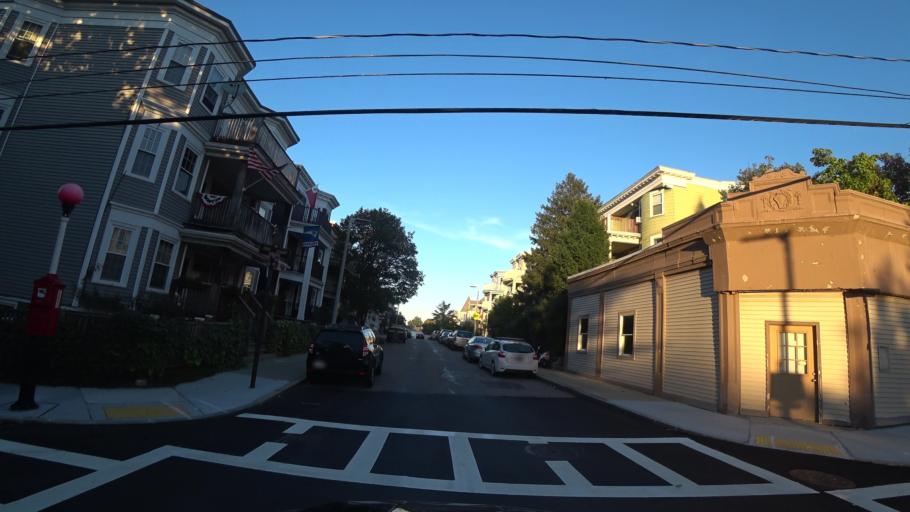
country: US
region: Massachusetts
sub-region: Suffolk County
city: South Boston
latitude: 42.2937
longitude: -71.0547
